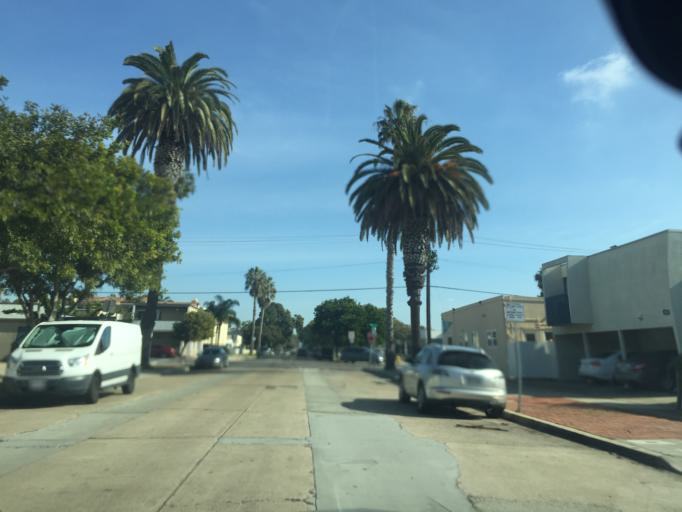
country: US
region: California
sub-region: San Diego County
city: La Jolla
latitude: 32.7943
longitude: -117.2516
